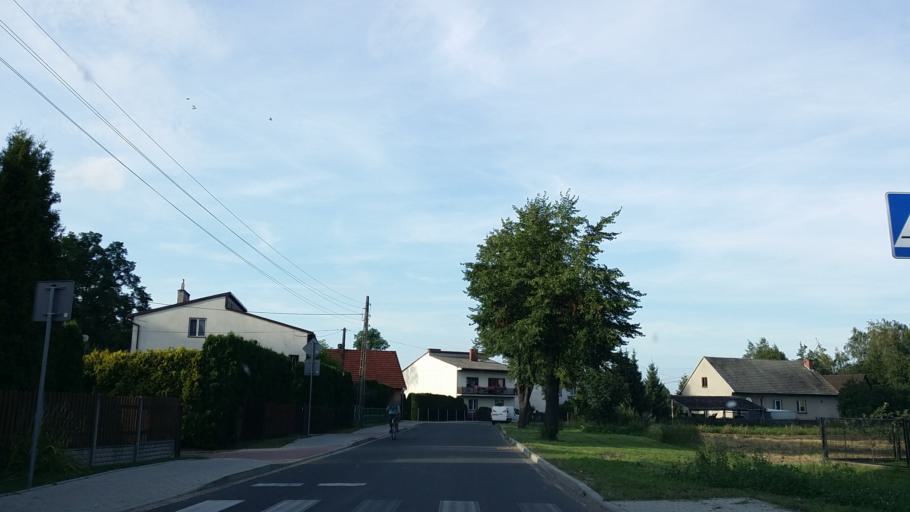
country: PL
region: Lesser Poland Voivodeship
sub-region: Powiat oswiecimski
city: Zator
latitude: 49.9878
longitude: 19.4173
